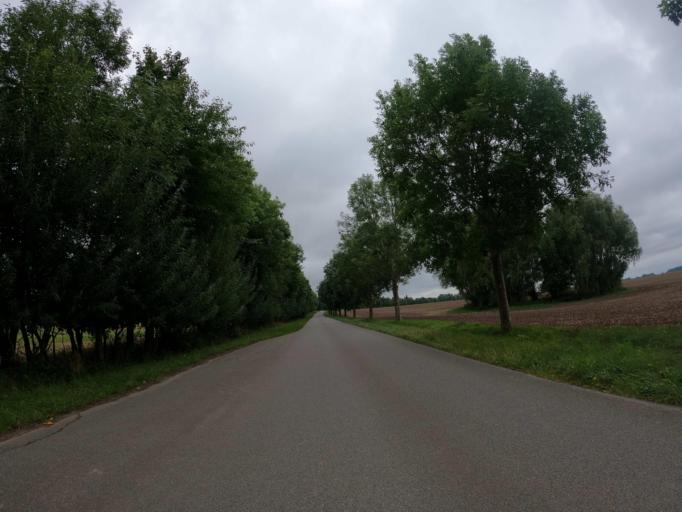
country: DE
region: Mecklenburg-Vorpommern
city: Garz
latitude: 54.3052
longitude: 13.3351
